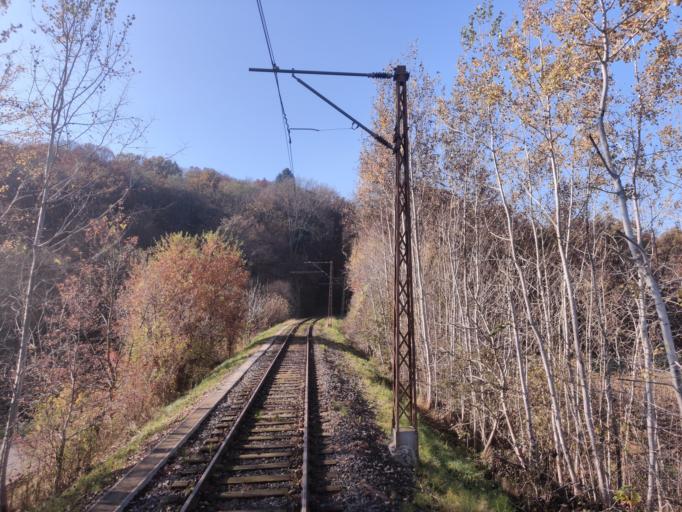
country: AT
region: Styria
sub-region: Politischer Bezirk Suedoststeiermark
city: Bad Gleichenberg
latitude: 46.8741
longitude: 15.8983
